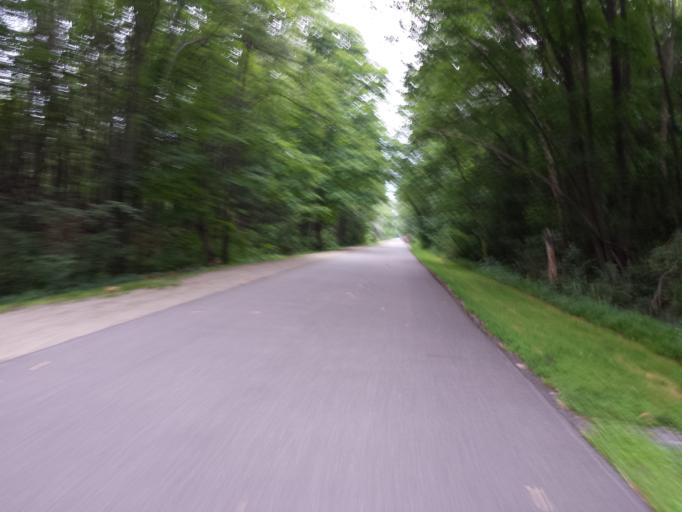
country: US
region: New York
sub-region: Dutchess County
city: Red Oaks Mill
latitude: 41.6350
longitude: -73.8582
